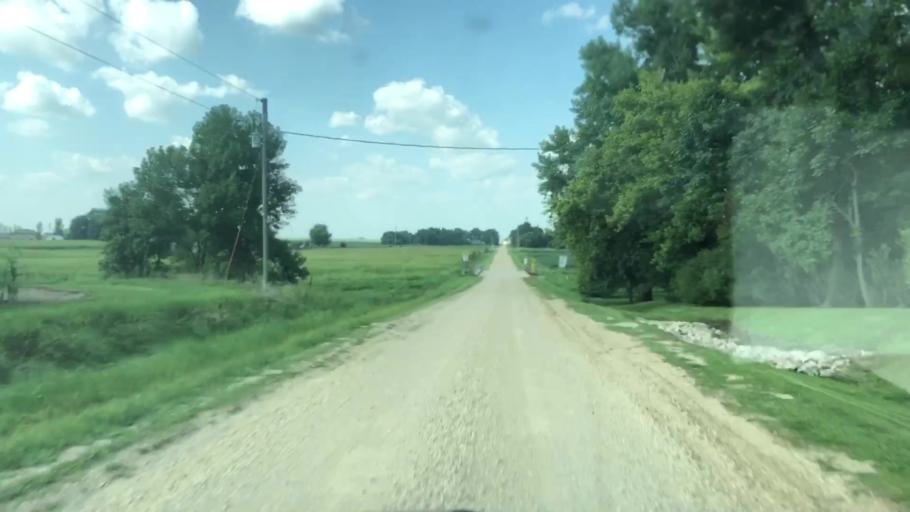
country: US
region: Iowa
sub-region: O'Brien County
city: Sheldon
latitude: 43.1667
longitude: -95.7823
